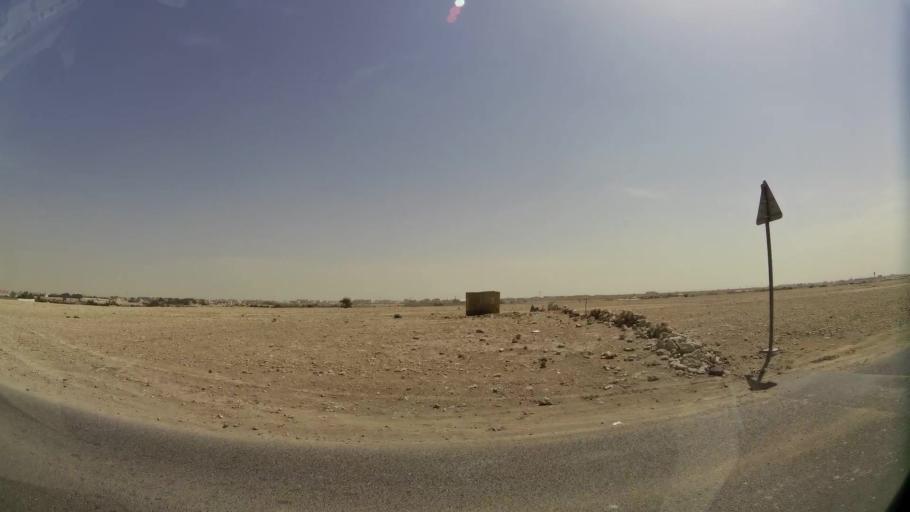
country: QA
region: Baladiyat ar Rayyan
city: Ar Rayyan
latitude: 25.2644
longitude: 51.3929
